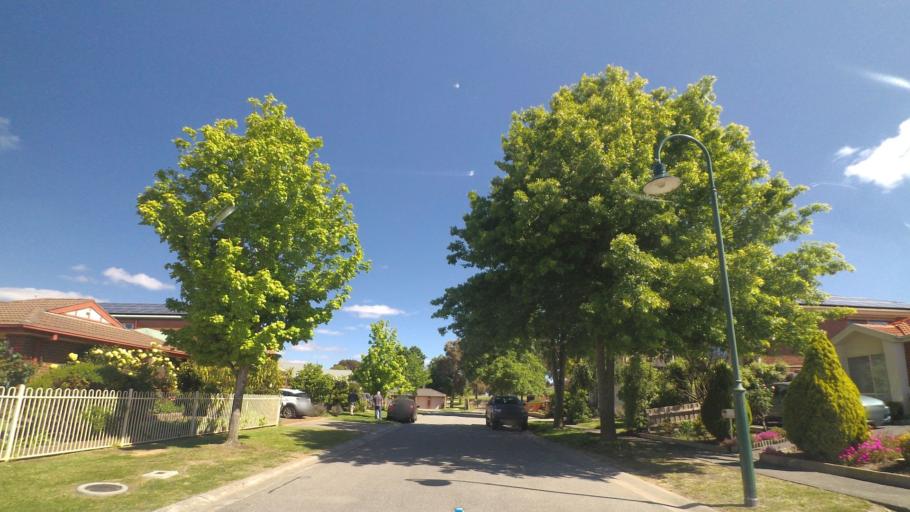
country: AU
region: Victoria
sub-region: Knox
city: Boronia
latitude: -37.8582
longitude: 145.2810
